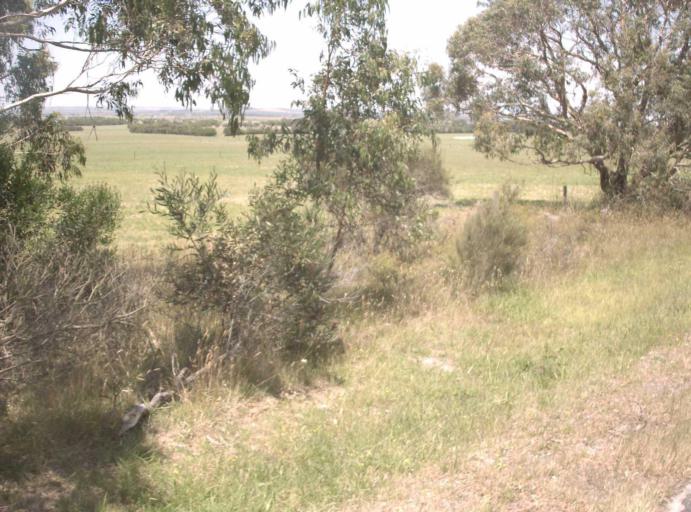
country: AU
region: Victoria
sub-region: Bass Coast
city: North Wonthaggi
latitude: -38.6516
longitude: 145.9369
